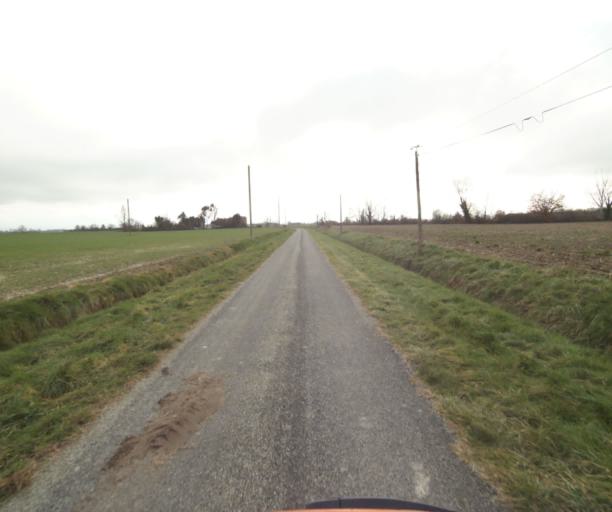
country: FR
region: Midi-Pyrenees
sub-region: Departement de l'Ariege
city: Mazeres
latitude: 43.2029
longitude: 1.6794
